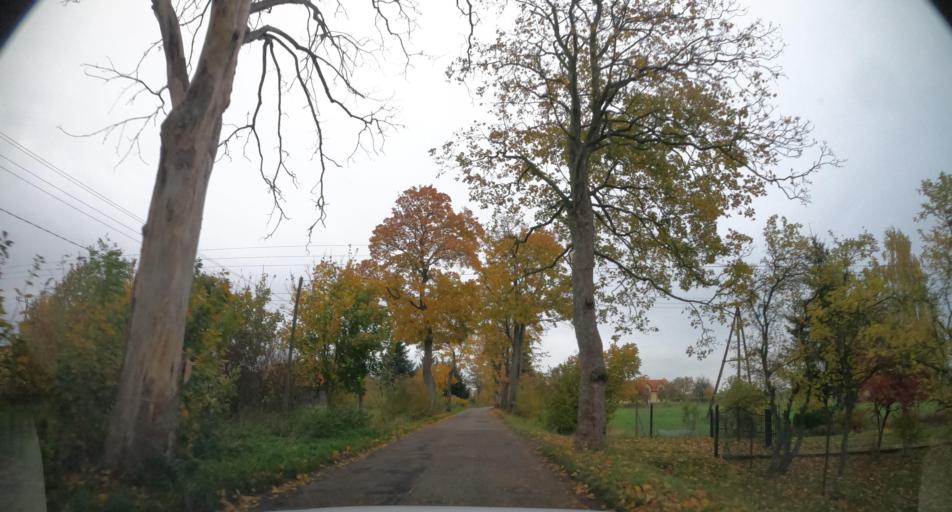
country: PL
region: West Pomeranian Voivodeship
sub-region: Powiat kamienski
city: Wolin
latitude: 53.9147
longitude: 14.6108
